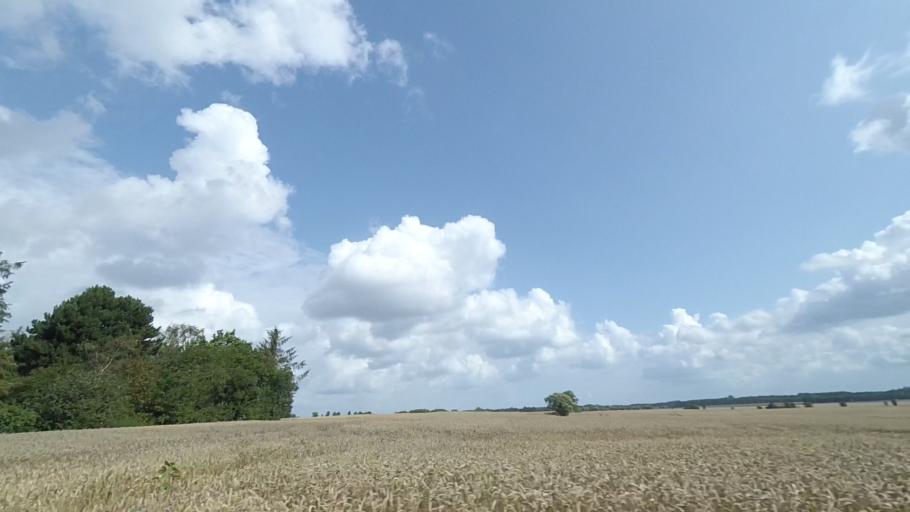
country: DK
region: Central Jutland
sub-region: Norddjurs Kommune
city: Allingabro
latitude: 56.5034
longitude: 10.3745
